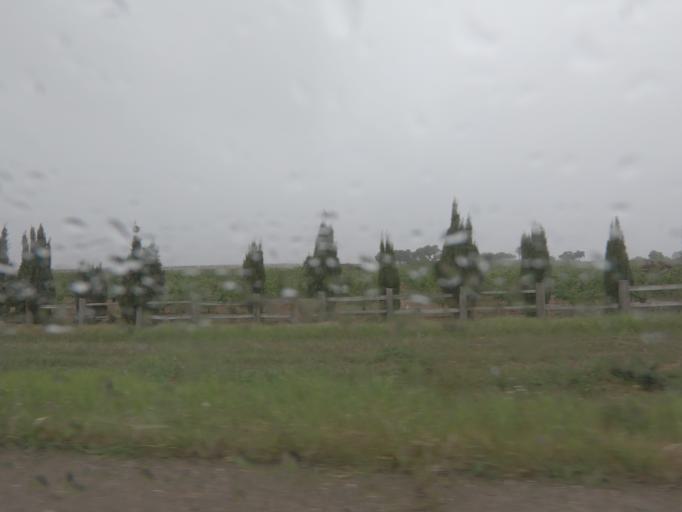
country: ES
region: Extremadura
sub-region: Provincia de Badajoz
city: Badajoz
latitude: 38.9412
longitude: -6.9198
